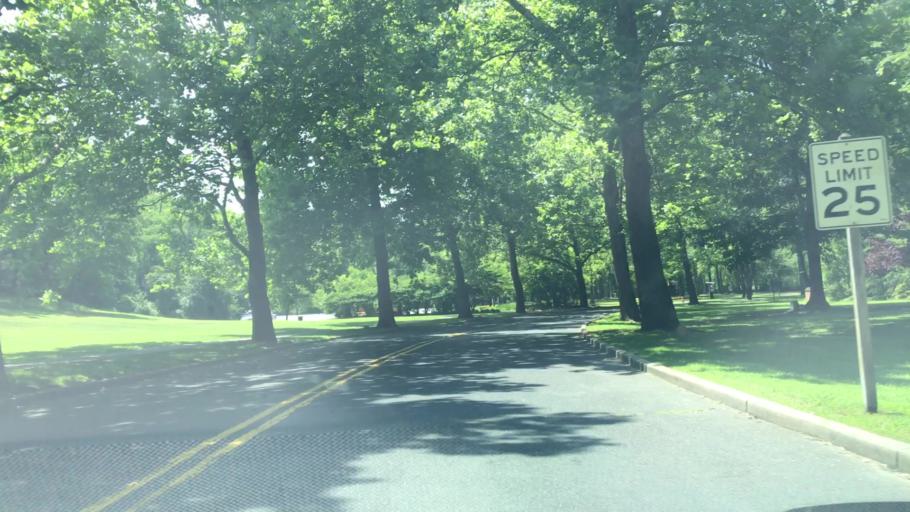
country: US
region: New Jersey
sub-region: Bergen County
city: River Edge
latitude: 40.9311
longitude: -74.0467
